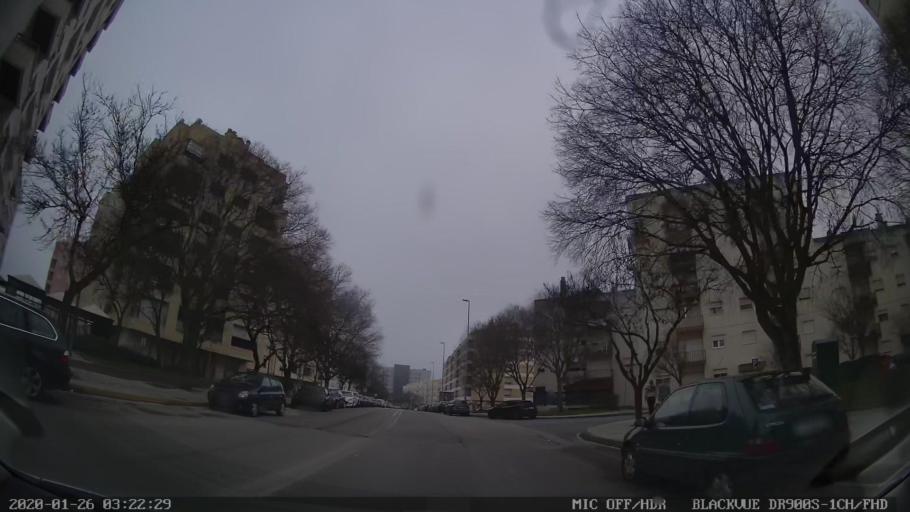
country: PT
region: Santarem
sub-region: Santarem
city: Santarem
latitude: 39.2256
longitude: -8.6904
